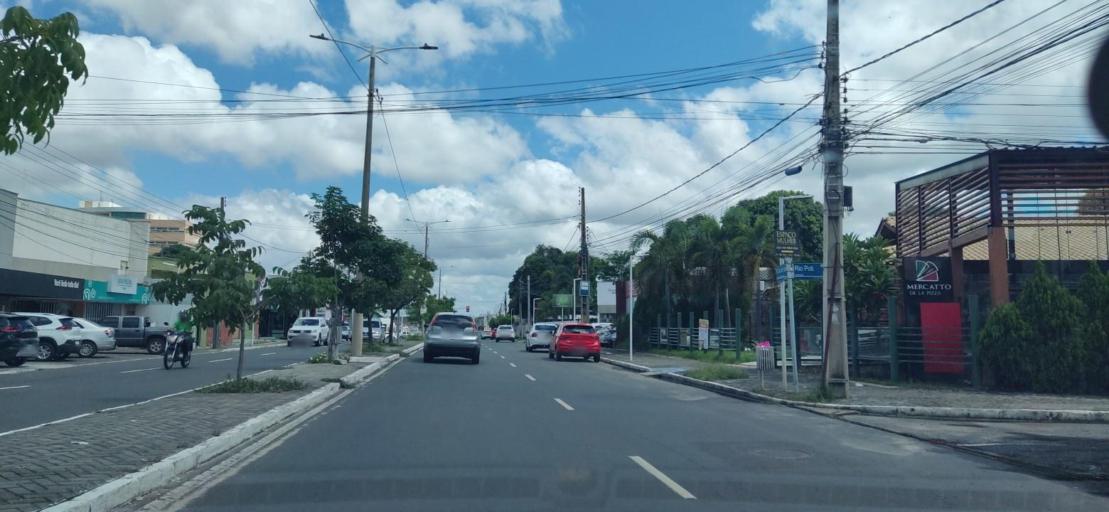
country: BR
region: Piaui
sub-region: Teresina
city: Teresina
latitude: -5.0688
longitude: -42.7927
